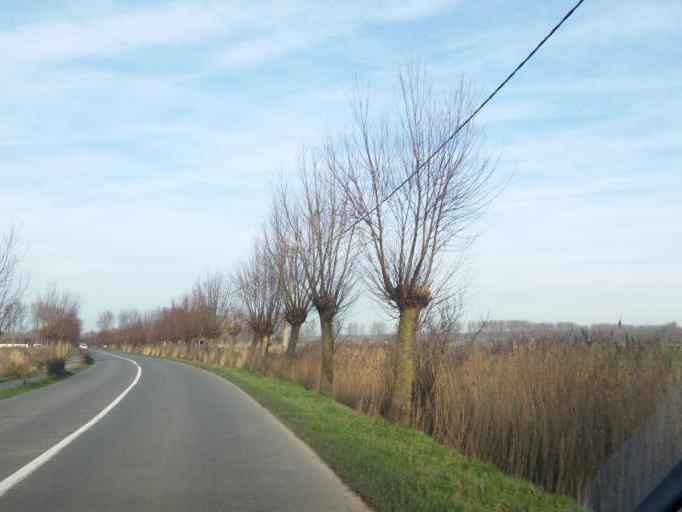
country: BE
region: Flanders
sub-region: Provincie West-Vlaanderen
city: Damme
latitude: 51.2578
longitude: 3.2758
